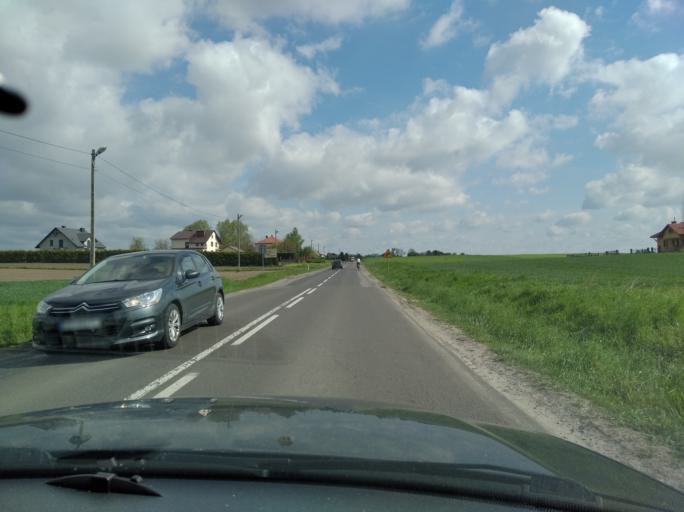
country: PL
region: Subcarpathian Voivodeship
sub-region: Powiat przeworski
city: Urzejowice
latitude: 50.0216
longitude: 22.4632
